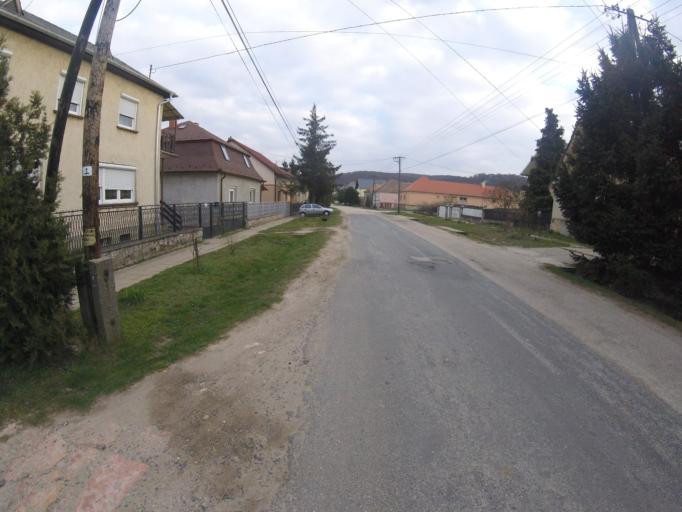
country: HU
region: Komarom-Esztergom
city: Oroszlany
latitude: 47.4759
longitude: 18.3962
